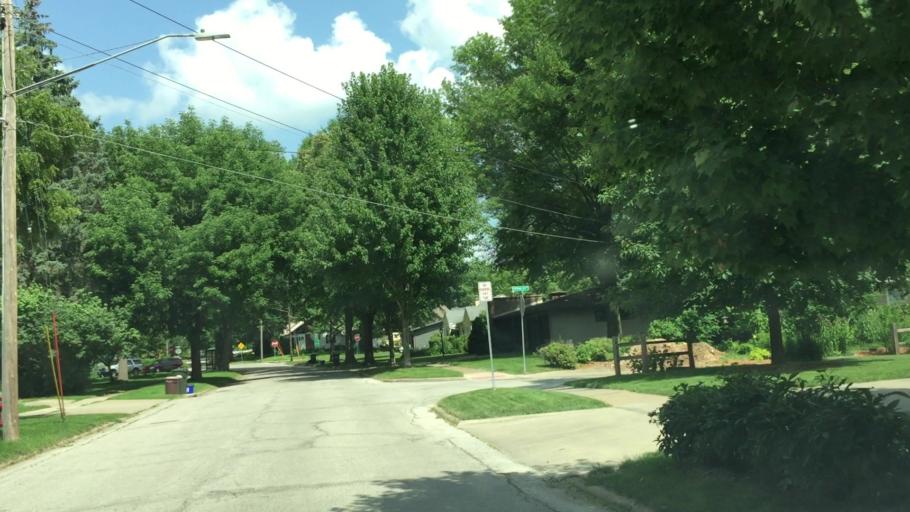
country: US
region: Iowa
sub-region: Johnson County
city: Iowa City
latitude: 41.6588
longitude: -91.5133
